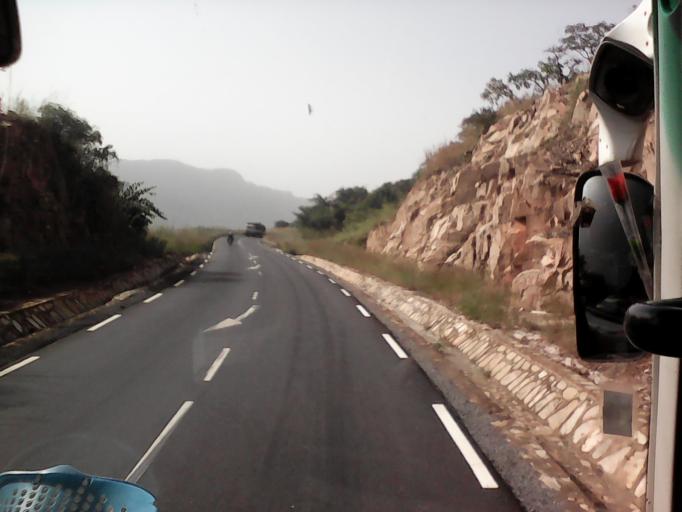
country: TG
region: Kara
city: Bafilo
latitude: 9.2652
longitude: 1.2320
